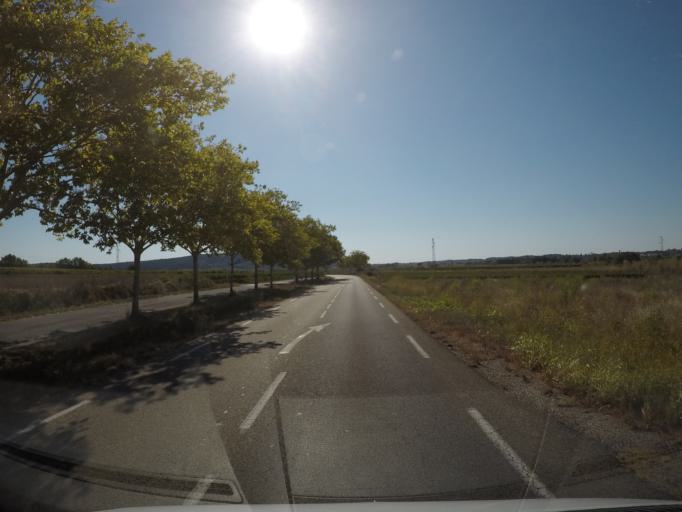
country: FR
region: Languedoc-Roussillon
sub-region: Departement du Gard
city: Ledignan
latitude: 44.0123
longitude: 4.1113
